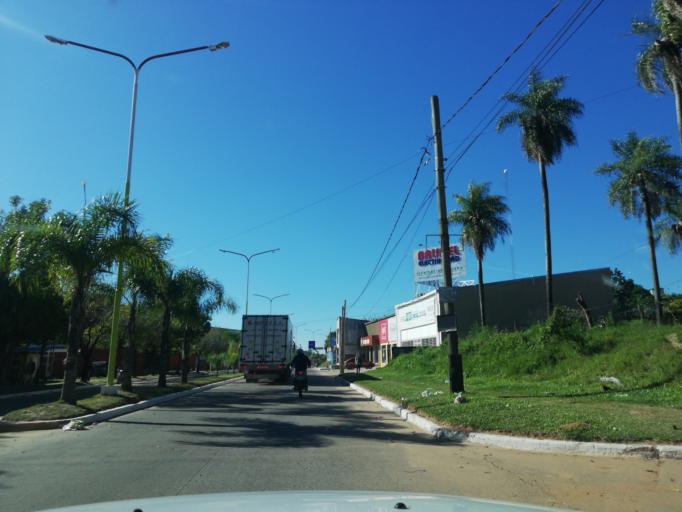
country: AR
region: Corrientes
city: Corrientes
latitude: -27.4770
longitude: -58.7873
